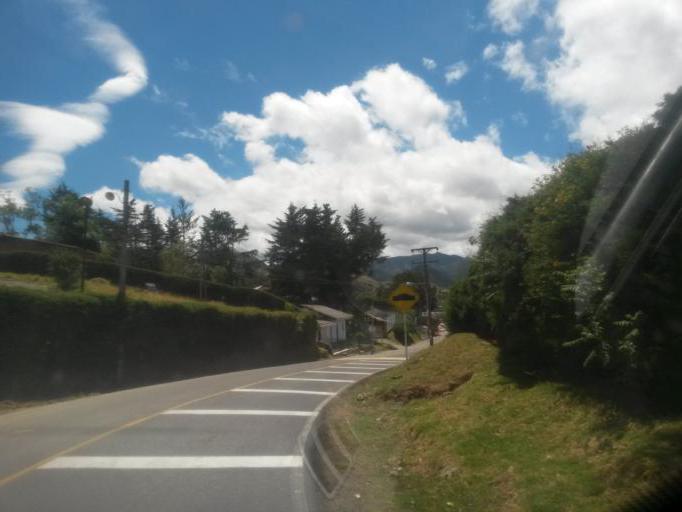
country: CO
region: Cauca
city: Silvia
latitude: 2.6082
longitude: -76.3870
